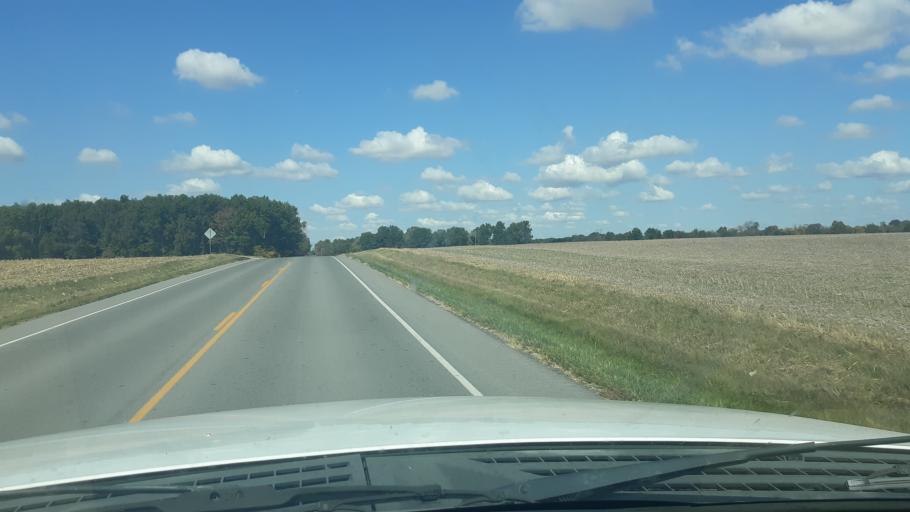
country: US
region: Illinois
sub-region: Saline County
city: Eldorado
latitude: 37.8056
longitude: -88.4847
